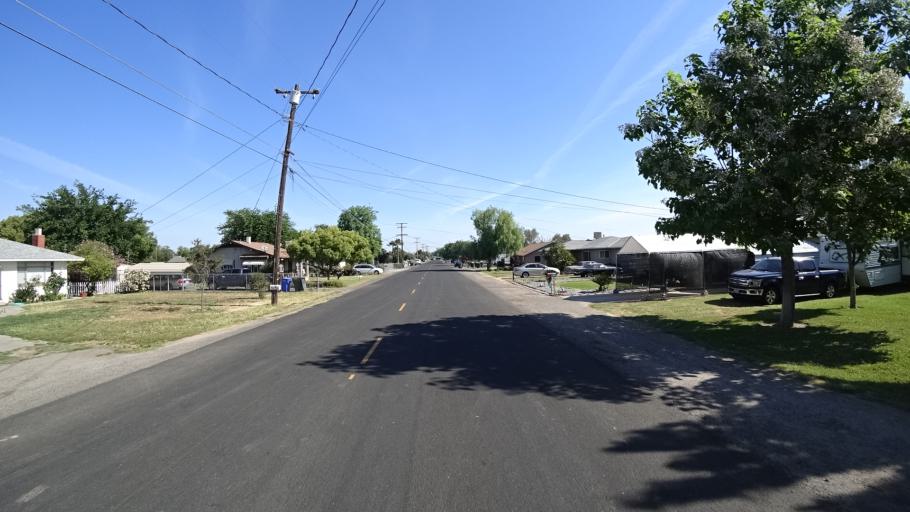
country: US
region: California
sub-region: Kings County
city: Hanford
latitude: 36.3394
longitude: -119.6350
